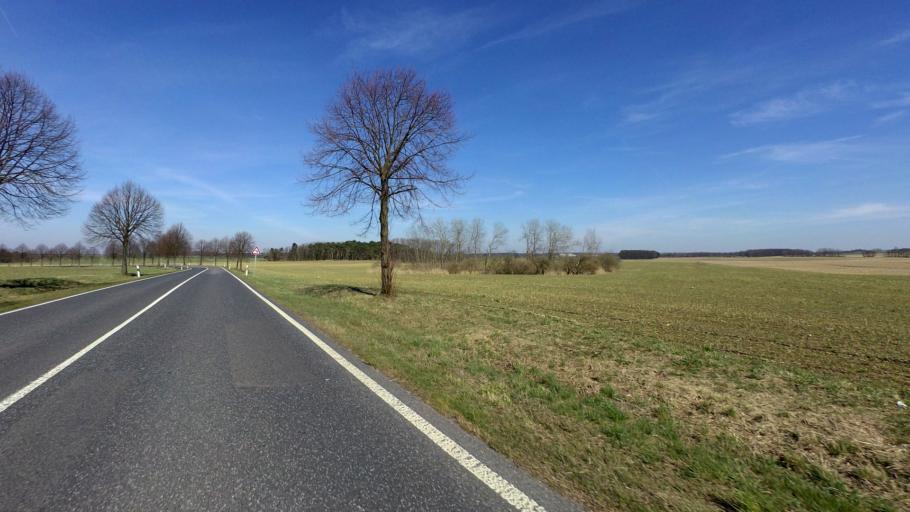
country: DE
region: Brandenburg
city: Furstenwalde
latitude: 52.4419
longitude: 14.0515
